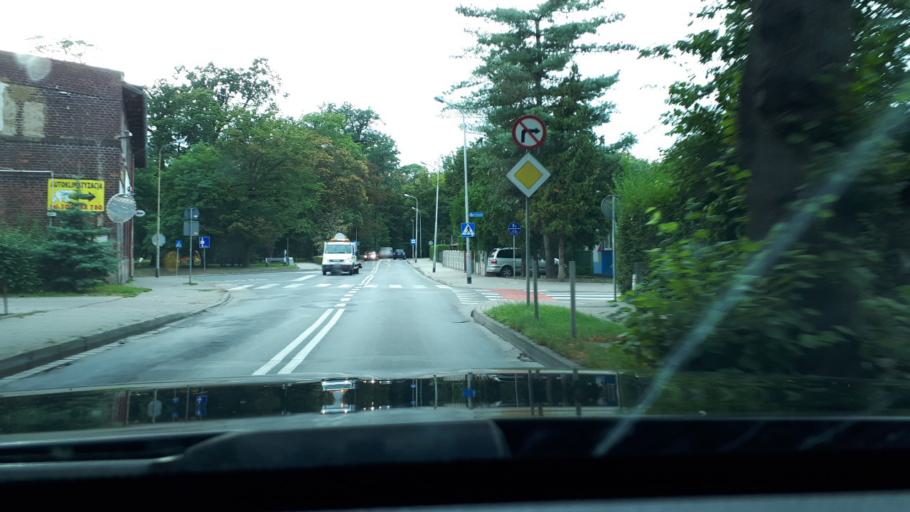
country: PL
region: Lower Silesian Voivodeship
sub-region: Powiat olesnicki
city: Olesnica
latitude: 51.2064
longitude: 17.3771
